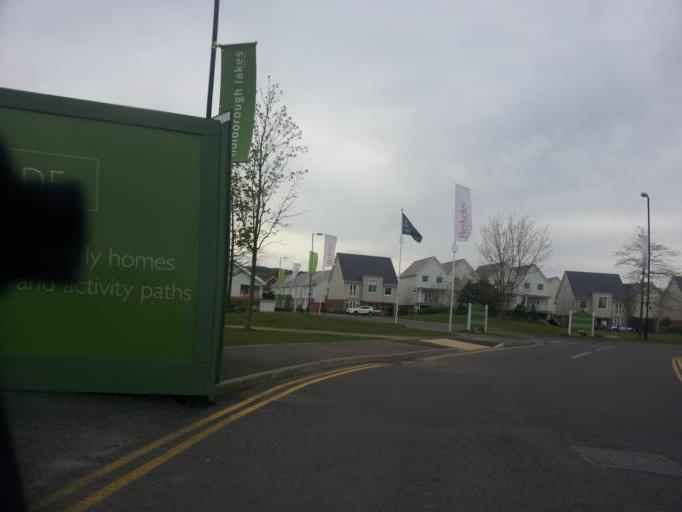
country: GB
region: England
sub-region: Kent
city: Snodland
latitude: 51.3361
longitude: 0.4411
